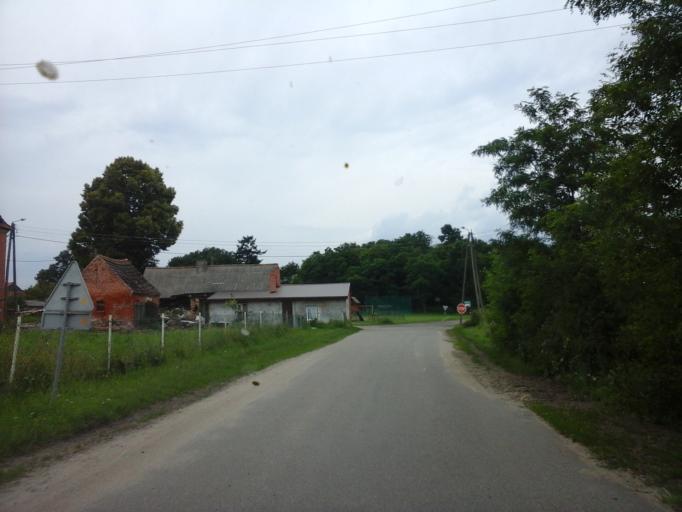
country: PL
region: West Pomeranian Voivodeship
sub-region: Powiat choszczenski
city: Bierzwnik
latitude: 53.0558
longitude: 15.5950
